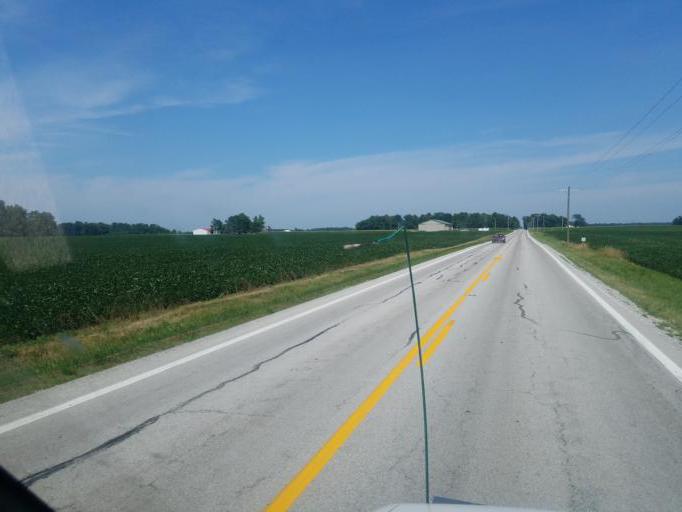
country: US
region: Ohio
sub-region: Shelby County
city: Botkins
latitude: 40.4967
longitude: -84.2295
